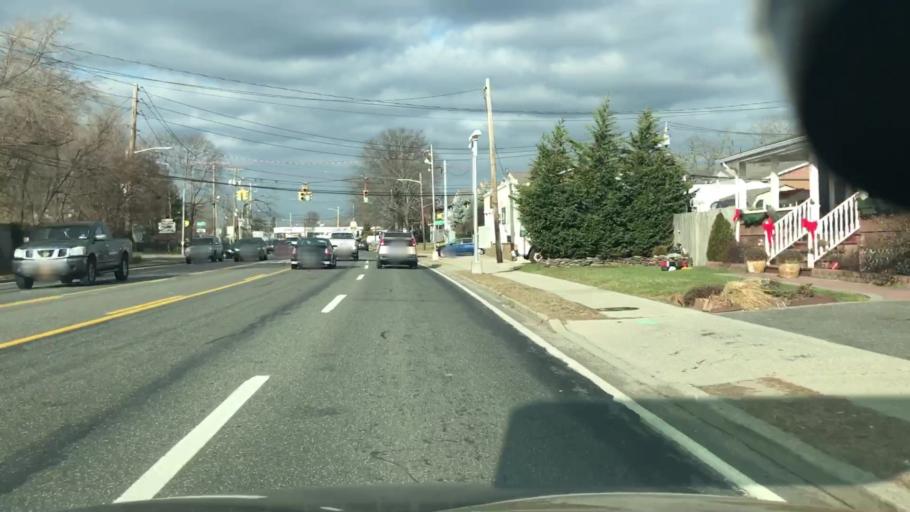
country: US
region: New York
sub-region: Suffolk County
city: Babylon
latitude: 40.6997
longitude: -73.3425
